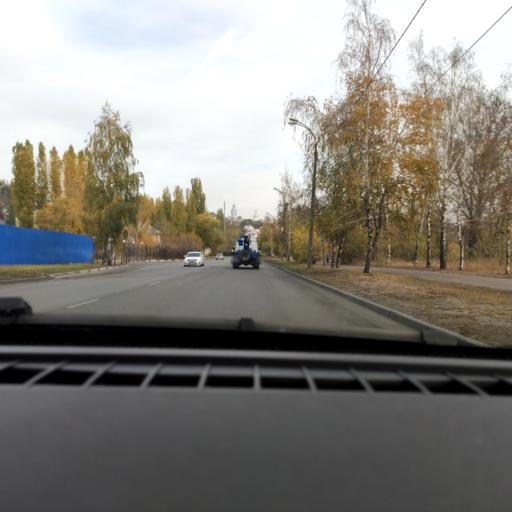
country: RU
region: Voronezj
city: Voronezh
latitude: 51.6529
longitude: 39.2119
